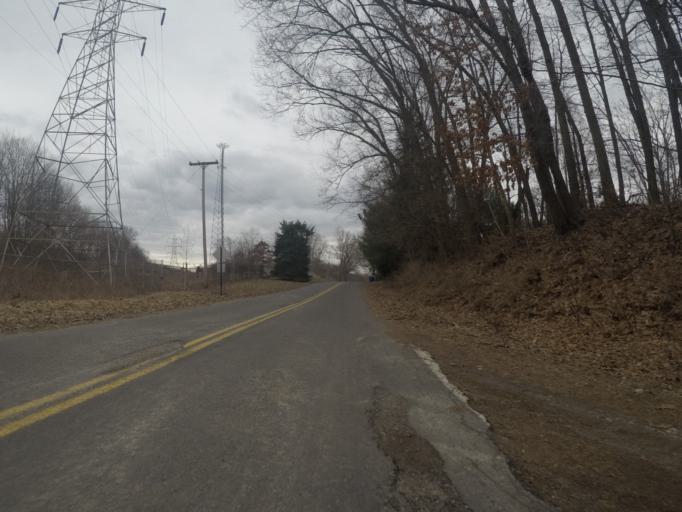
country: US
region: Ohio
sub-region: Portage County
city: Kent
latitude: 41.1714
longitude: -81.3120
